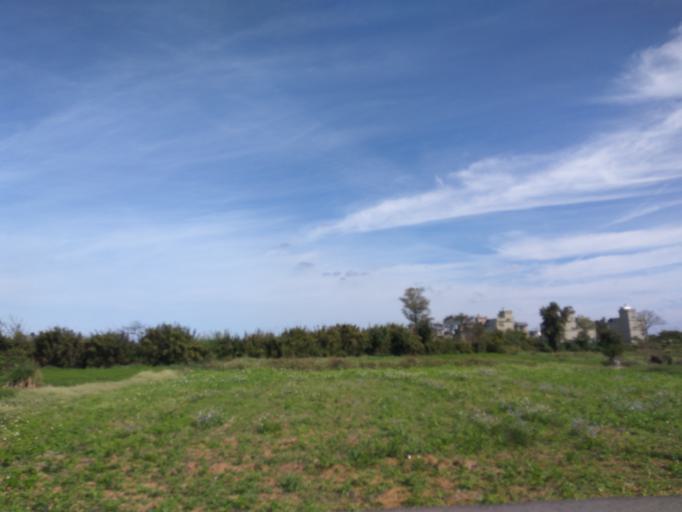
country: TW
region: Taiwan
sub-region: Hsinchu
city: Zhubei
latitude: 25.0150
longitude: 121.0889
